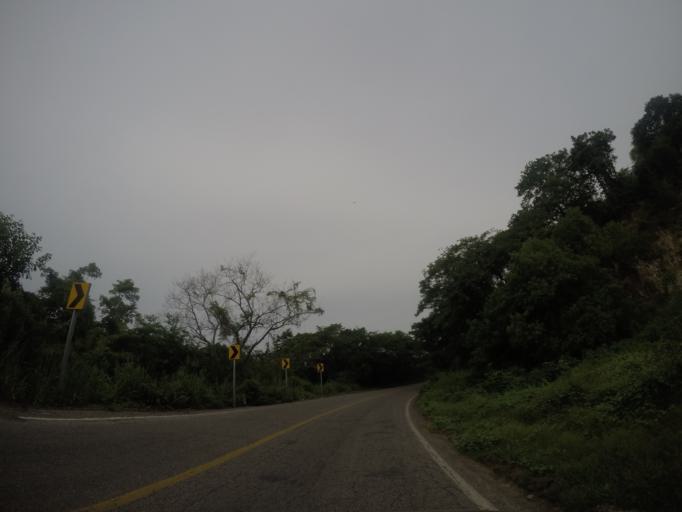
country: MX
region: Oaxaca
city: San Pedro Mixtepec
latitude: 15.9537
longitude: -97.2226
